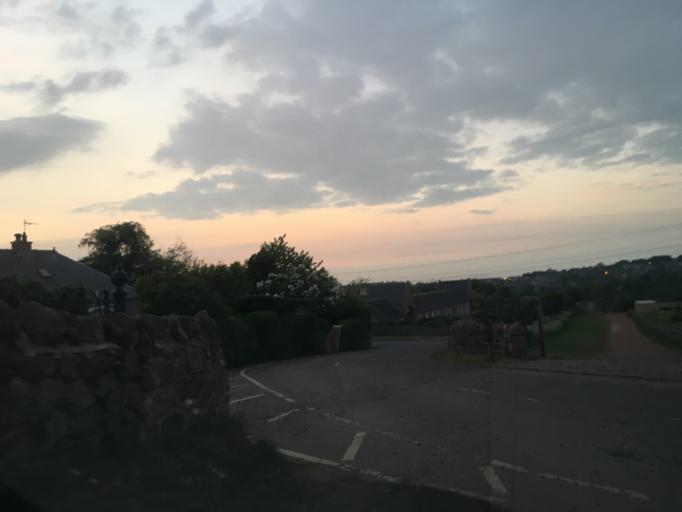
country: GB
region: Scotland
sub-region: Edinburgh
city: Colinton
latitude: 55.8937
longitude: -3.2169
